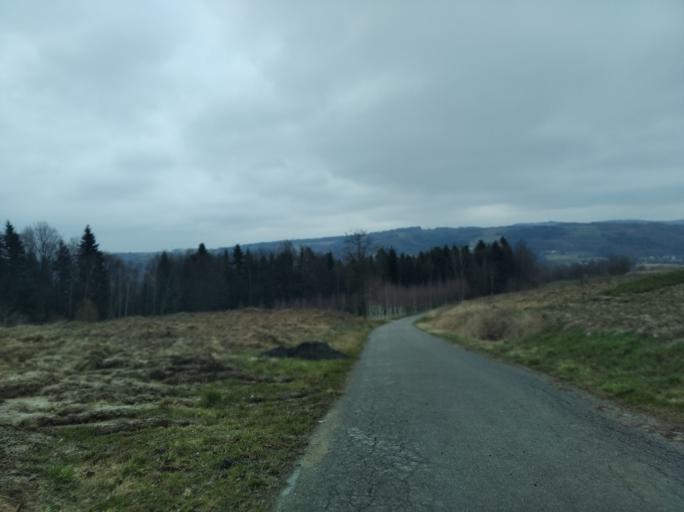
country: PL
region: Subcarpathian Voivodeship
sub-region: Powiat strzyzowski
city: Strzyzow
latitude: 49.9028
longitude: 21.8136
